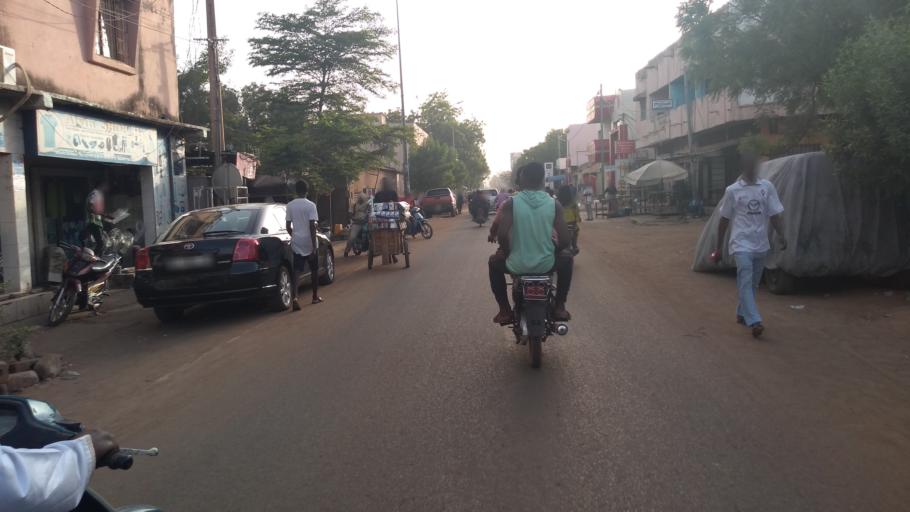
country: ML
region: Bamako
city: Bamako
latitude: 12.6450
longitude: -8.0106
